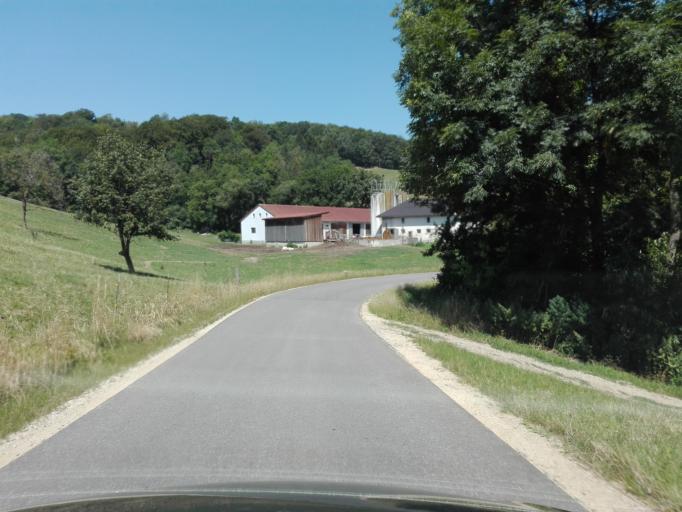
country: AT
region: Upper Austria
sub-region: Politischer Bezirk Urfahr-Umgebung
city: Steyregg
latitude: 48.3105
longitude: 14.3904
